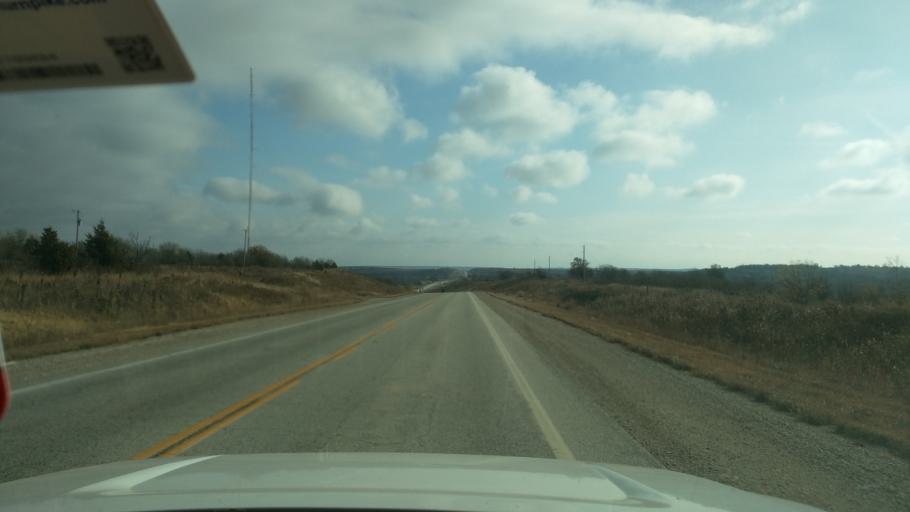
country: US
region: Kansas
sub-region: Chautauqua County
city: Sedan
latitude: 37.0834
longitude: -96.1919
